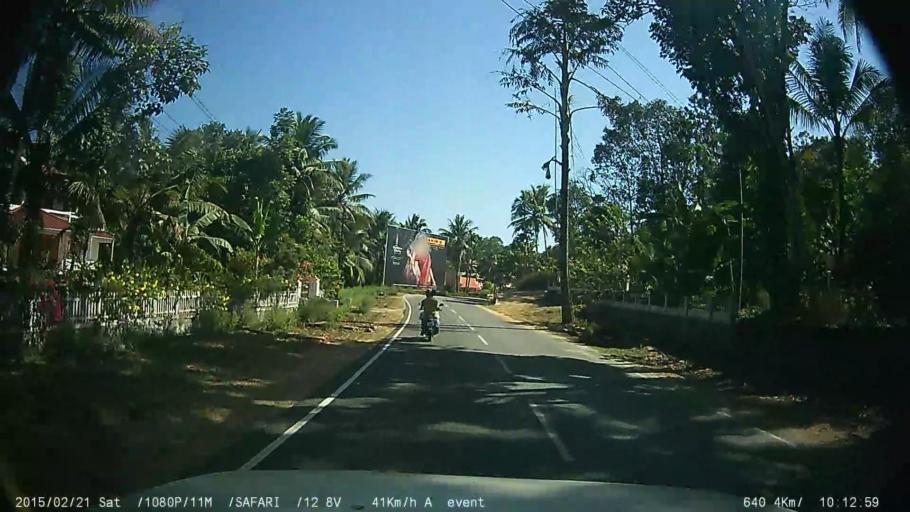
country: IN
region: Kerala
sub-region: Ernakulam
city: Muvattupuzha
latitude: 9.8865
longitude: 76.6270
